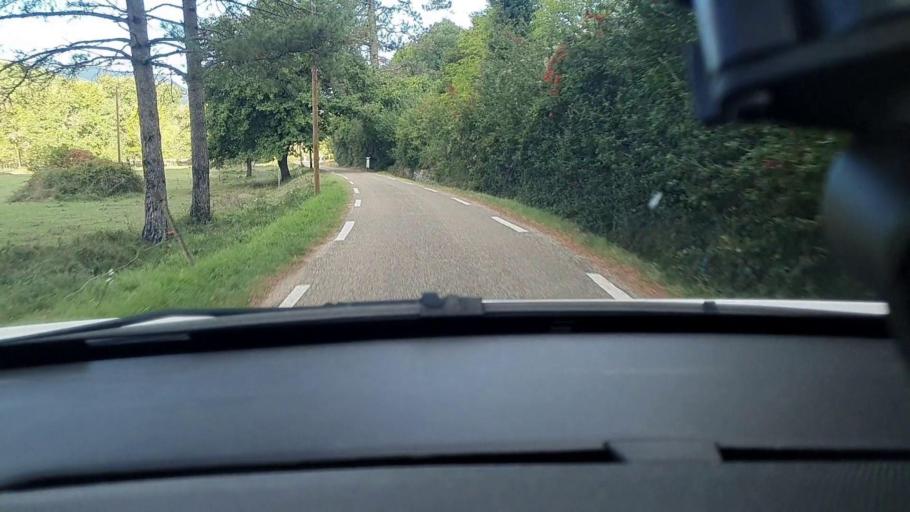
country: FR
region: Languedoc-Roussillon
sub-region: Departement du Gard
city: Besseges
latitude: 44.3269
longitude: 4.1189
